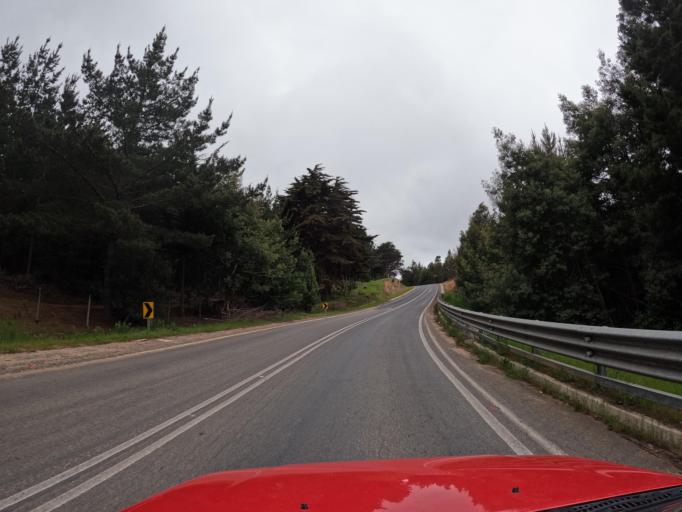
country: CL
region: O'Higgins
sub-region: Provincia de Colchagua
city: Santa Cruz
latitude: -34.5957
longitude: -72.0169
